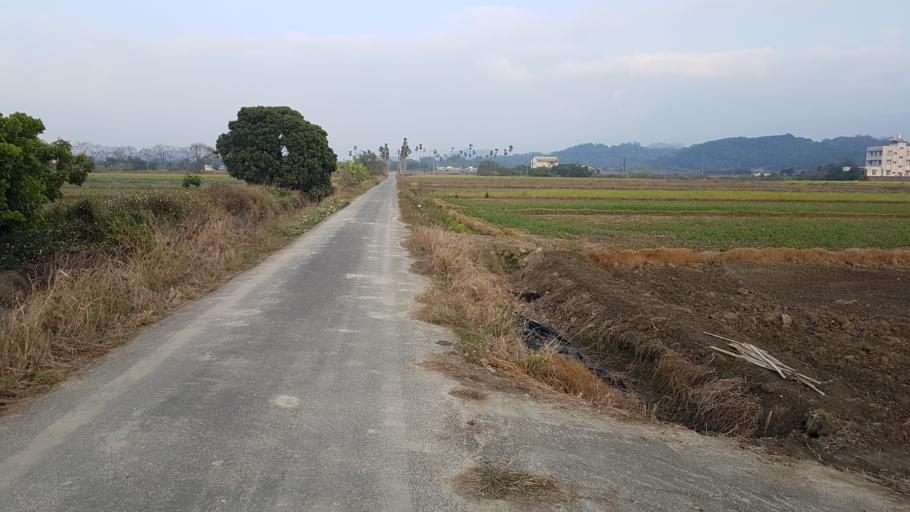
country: TW
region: Taiwan
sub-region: Chiayi
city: Jiayi Shi
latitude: 23.3737
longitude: 120.4510
